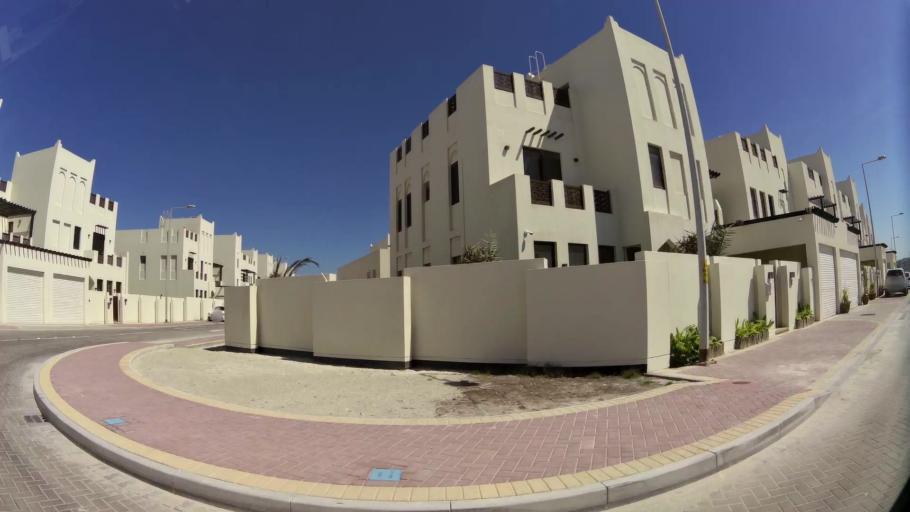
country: BH
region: Muharraq
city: Al Muharraq
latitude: 26.3025
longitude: 50.6356
